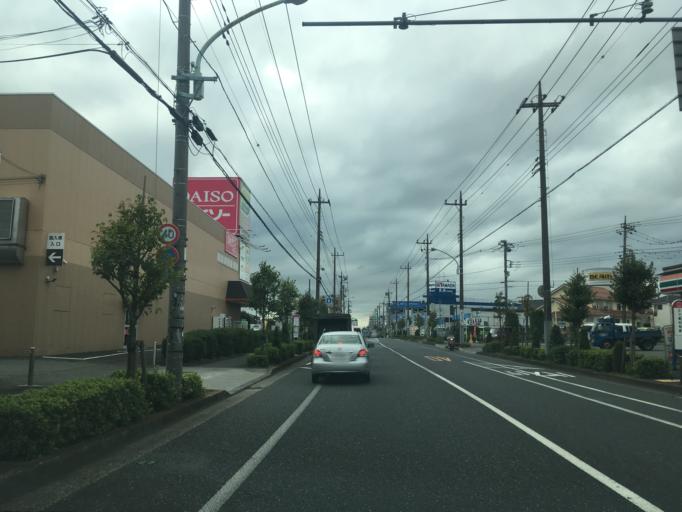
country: JP
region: Tokyo
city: Fussa
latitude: 35.7498
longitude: 139.3828
